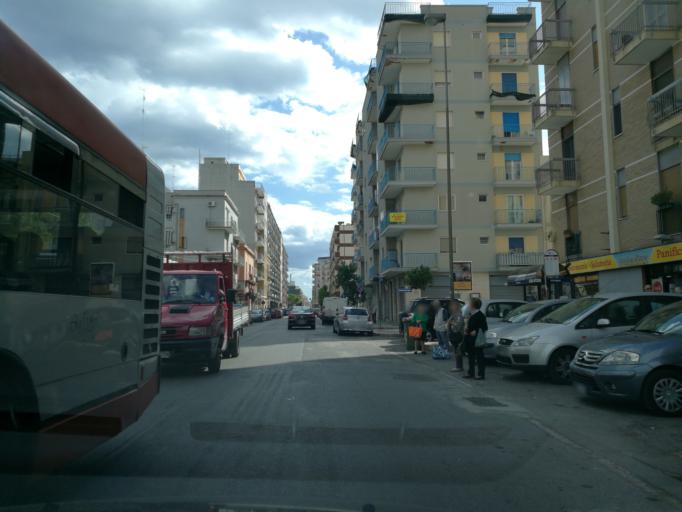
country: IT
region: Apulia
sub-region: Provincia di Bari
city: Bari
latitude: 41.1273
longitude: 16.8480
